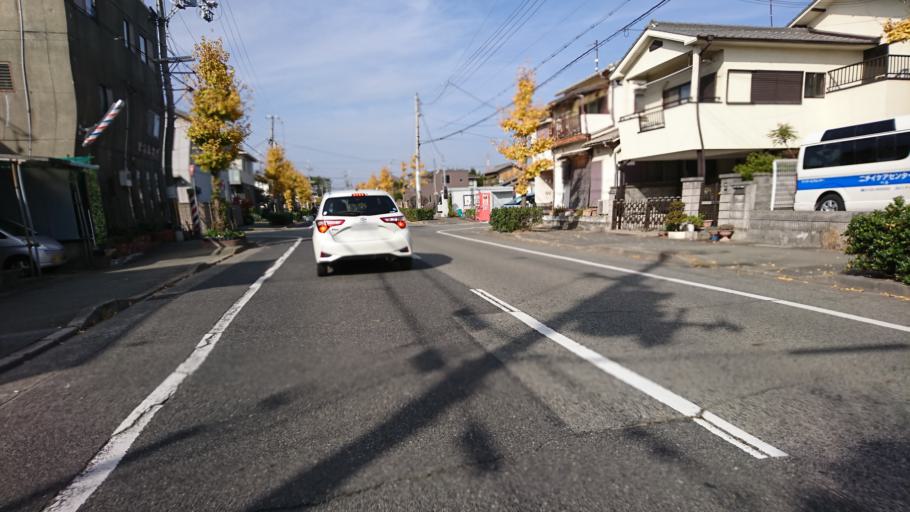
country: JP
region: Hyogo
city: Kakogawacho-honmachi
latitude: 34.7365
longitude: 134.8383
